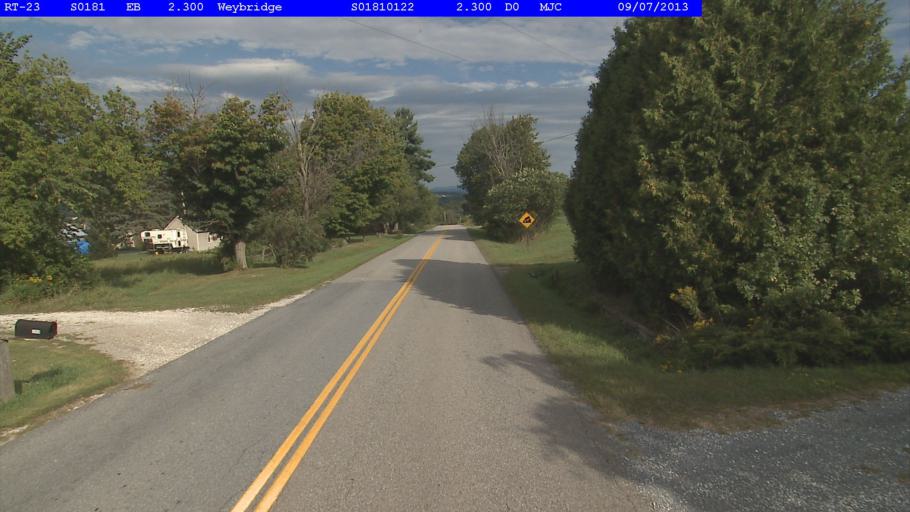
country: US
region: Vermont
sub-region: Addison County
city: Middlebury (village)
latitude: 44.0418
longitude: -73.2149
